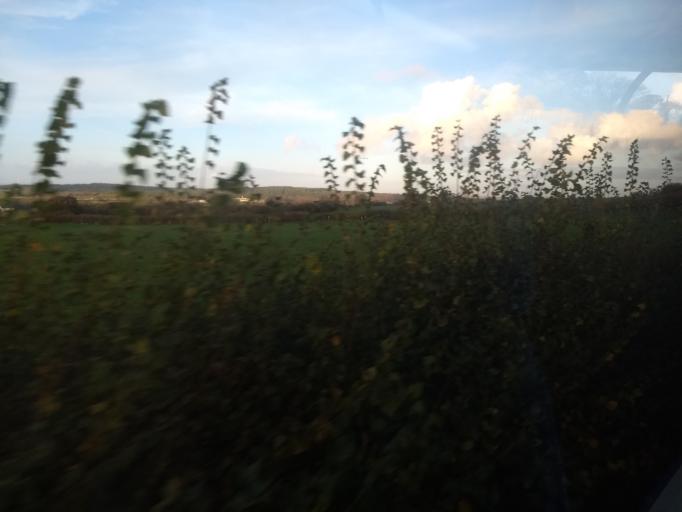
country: GB
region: England
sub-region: Isle of Wight
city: Newport
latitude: 50.6889
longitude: -1.3459
